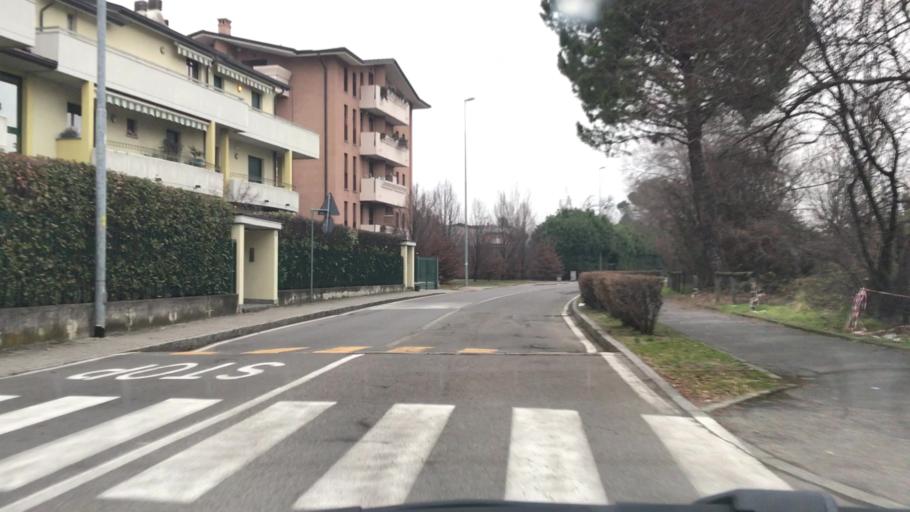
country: IT
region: Lombardy
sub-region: Provincia di Monza e Brianza
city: Seveso
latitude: 45.6444
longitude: 9.1454
